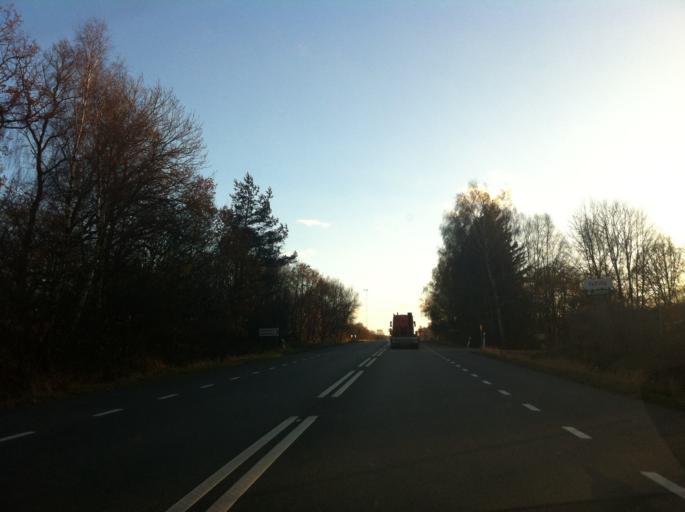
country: SE
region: Skane
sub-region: Hassleholms Kommun
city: Vinslov
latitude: 56.1837
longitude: 13.8717
